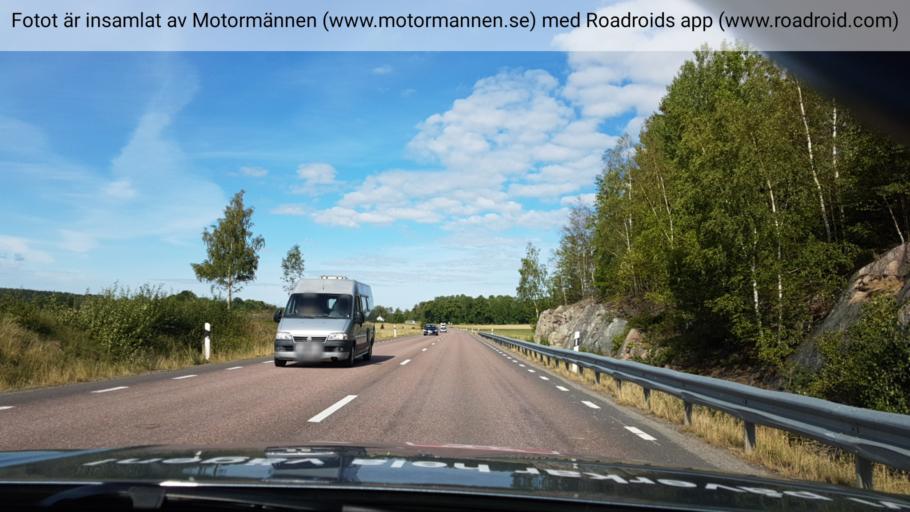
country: SE
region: Uppsala
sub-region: Osthammars Kommun
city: Bjorklinge
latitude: 59.9414
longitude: 17.4404
